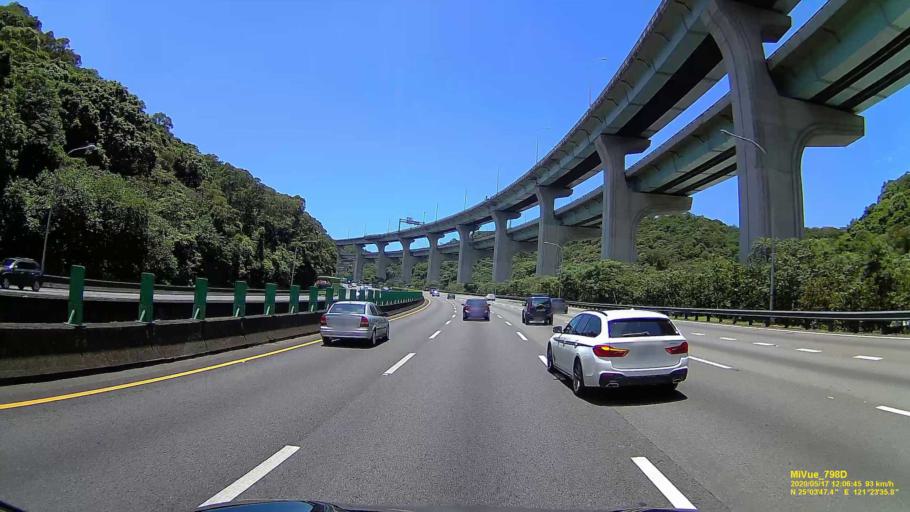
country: TW
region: Taipei
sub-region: Taipei
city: Banqiao
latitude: 25.0637
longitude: 121.3902
